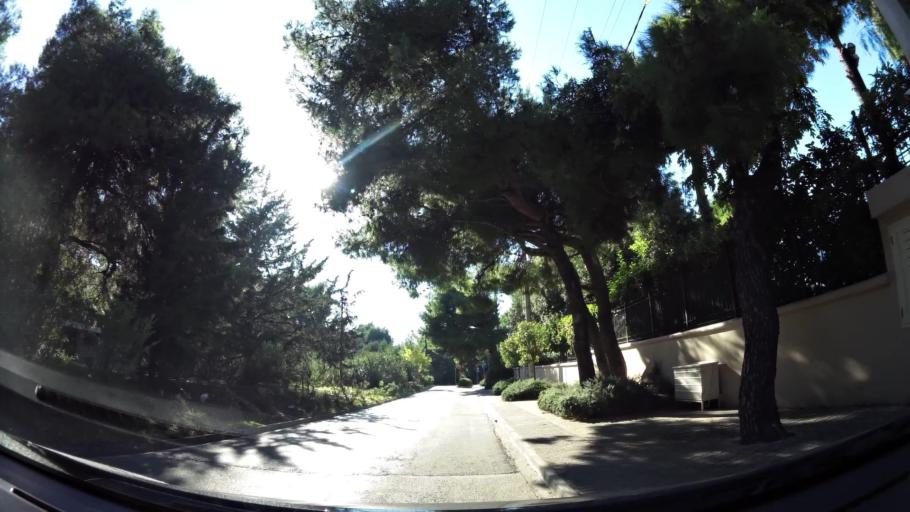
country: GR
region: Attica
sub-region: Nomarchia Athinas
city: Ekali
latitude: 38.1042
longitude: 23.8426
